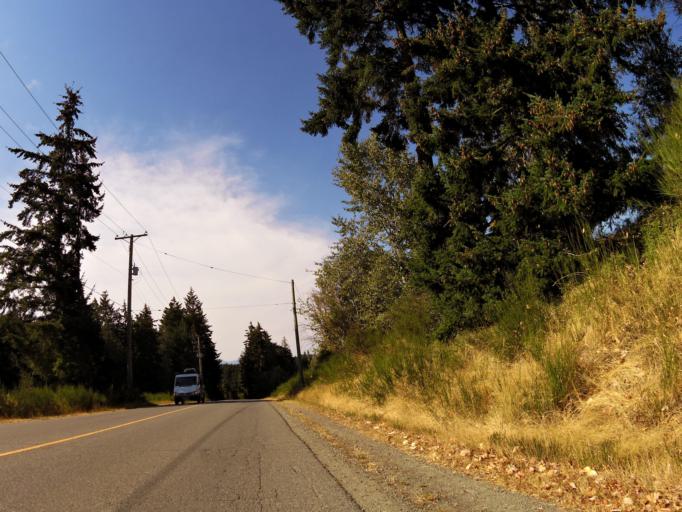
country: CA
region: British Columbia
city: North Saanich
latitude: 48.6879
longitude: -123.5544
